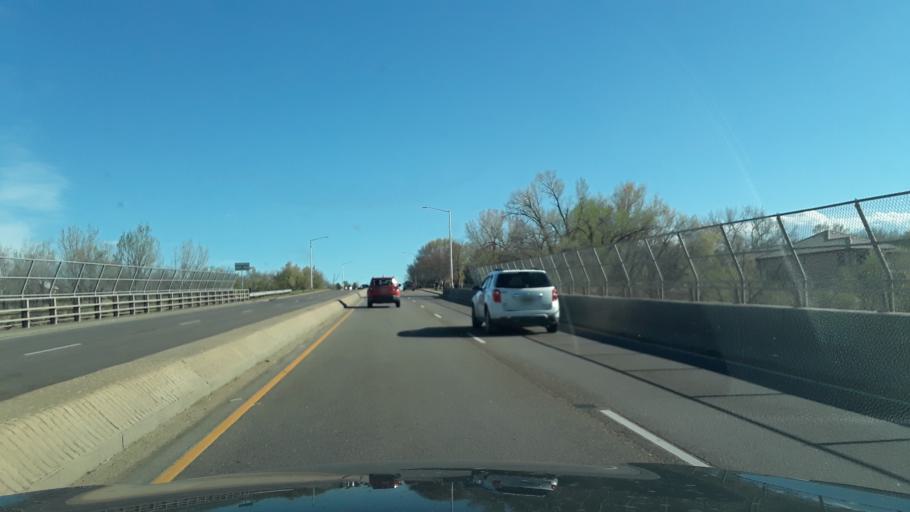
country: US
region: Colorado
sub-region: Pueblo County
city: Pueblo
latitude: 38.2685
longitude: -104.6622
